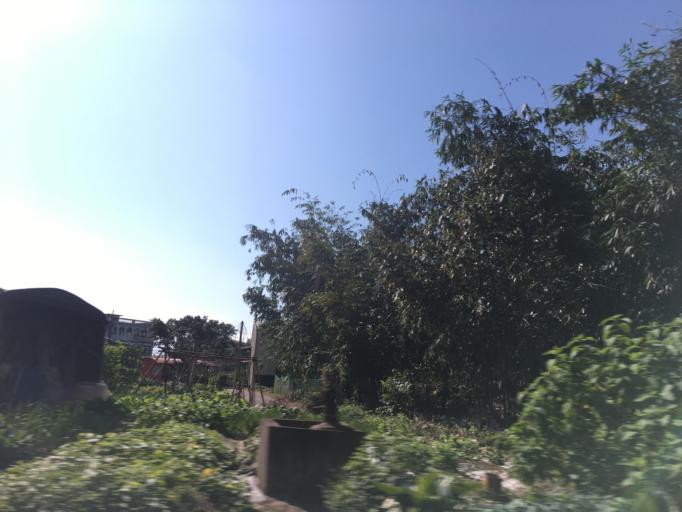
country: TW
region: Taiwan
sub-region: Yilan
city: Yilan
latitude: 24.7485
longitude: 121.7262
